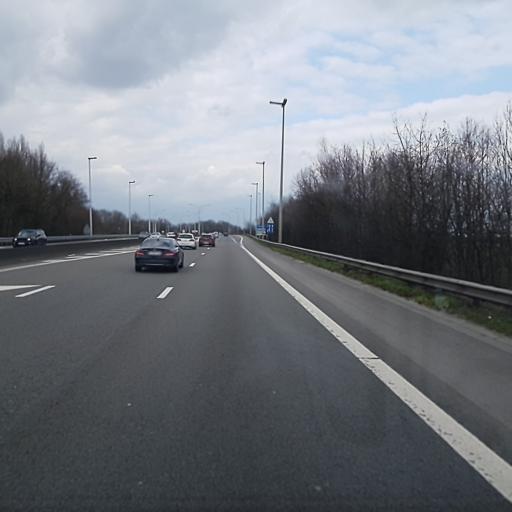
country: BE
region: Wallonia
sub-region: Province du Hainaut
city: Charleroi
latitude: 50.4477
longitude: 4.4425
